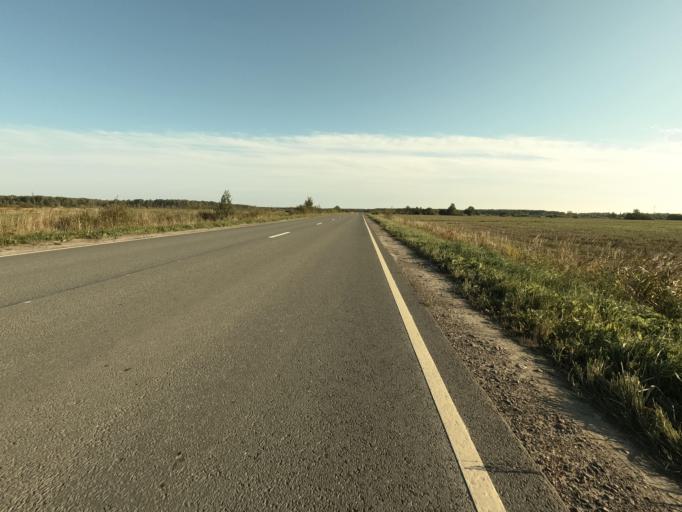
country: RU
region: St.-Petersburg
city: Sapernyy
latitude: 59.7413
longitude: 30.6503
